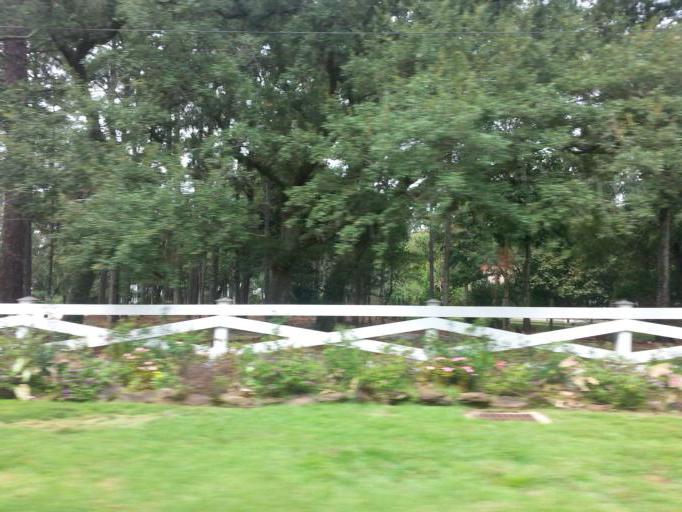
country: US
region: Alabama
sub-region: Baldwin County
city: Fairhope
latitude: 30.5050
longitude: -87.9214
